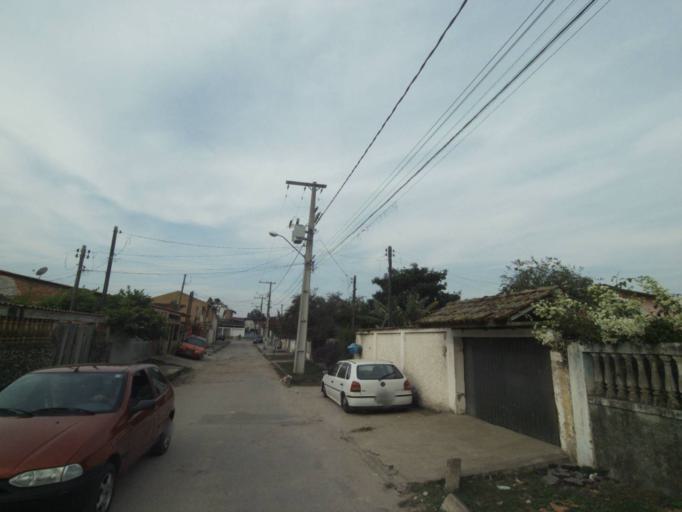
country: BR
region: Parana
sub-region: Paranagua
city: Paranagua
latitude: -25.5251
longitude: -48.5376
